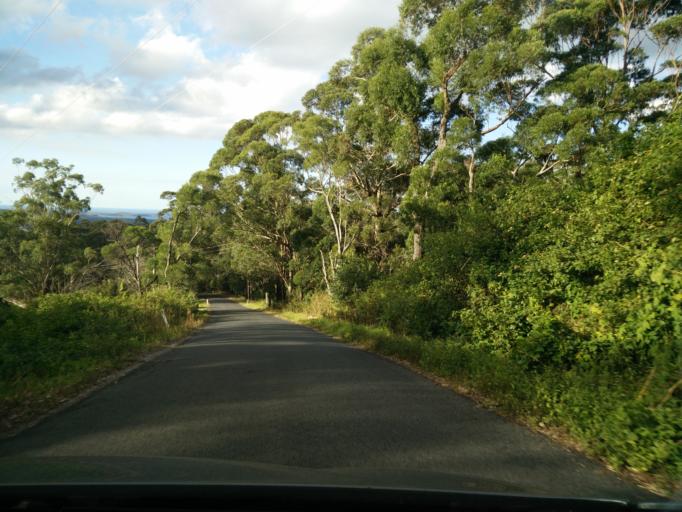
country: AU
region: New South Wales
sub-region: Kiama
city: Jamberoo
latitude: -34.6818
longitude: 150.7896
